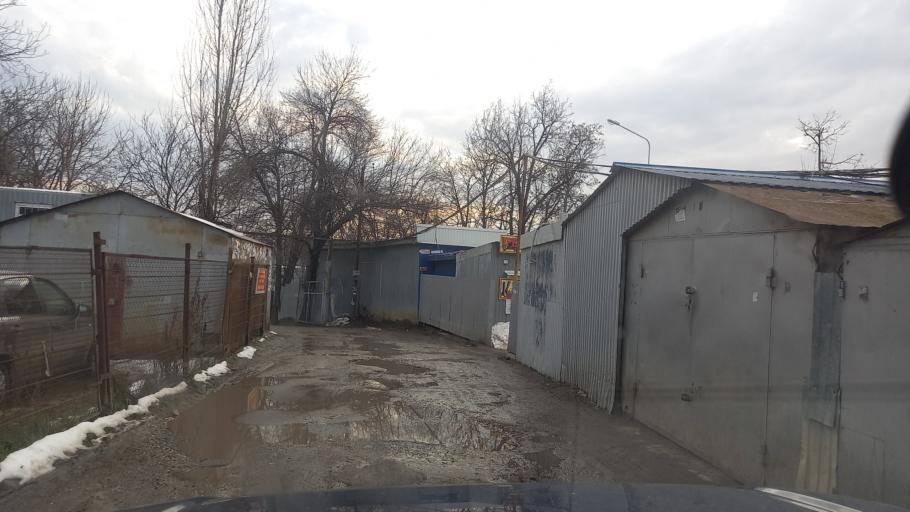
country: RU
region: Krasnodarskiy
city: Pashkovskiy
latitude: 45.0202
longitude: 39.0432
